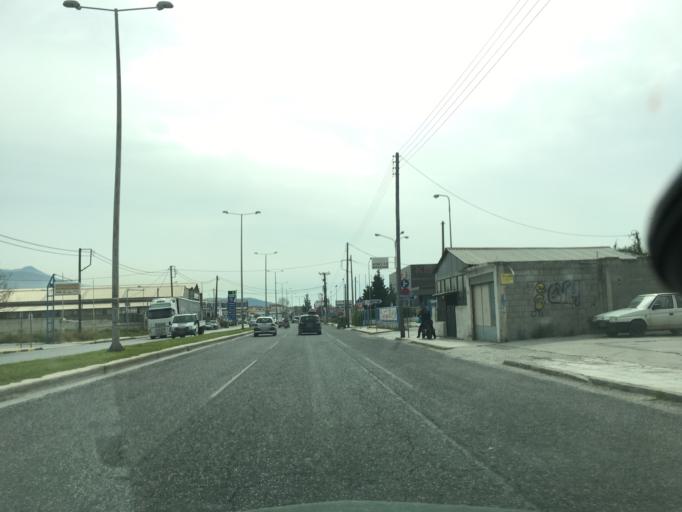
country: GR
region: Thessaly
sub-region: Nomos Magnisias
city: Nea Ionia
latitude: 39.3704
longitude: 22.9155
